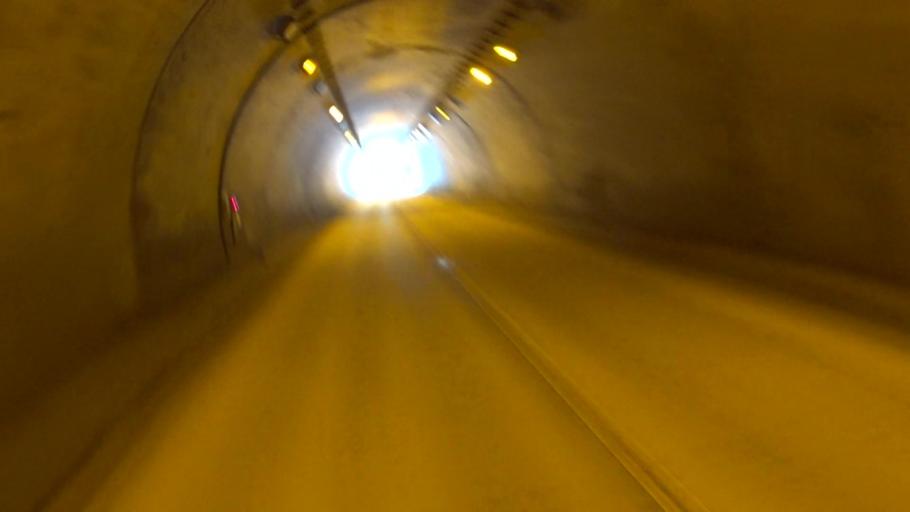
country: JP
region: Kyoto
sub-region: Kyoto-shi
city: Kamigyo-ku
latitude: 35.0822
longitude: 135.6870
